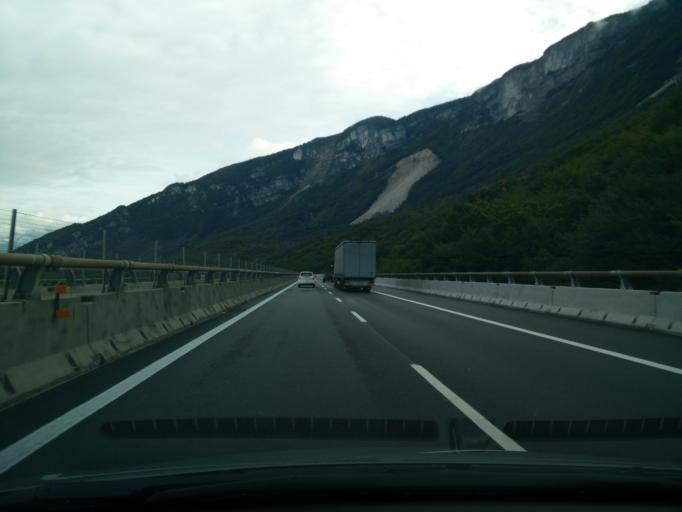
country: IT
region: Veneto
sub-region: Provincia di Treviso
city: Fregona
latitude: 46.0618
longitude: 12.3302
